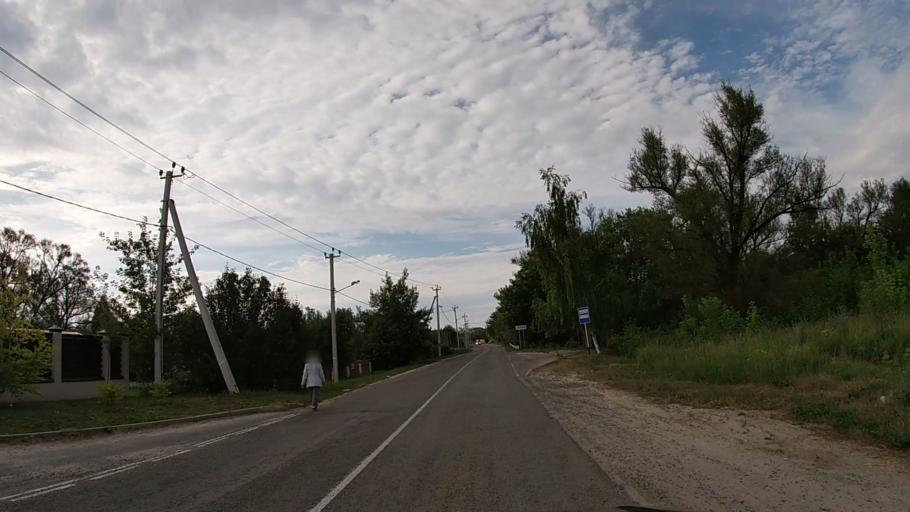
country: RU
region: Belgorod
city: Severnyy
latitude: 50.7111
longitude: 36.5978
